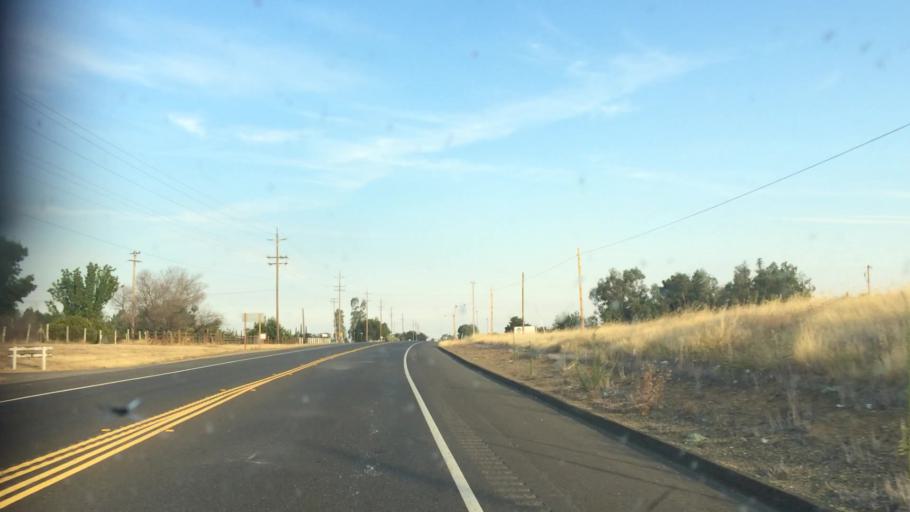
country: US
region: California
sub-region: Sacramento County
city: Wilton
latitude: 38.4987
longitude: -121.2080
